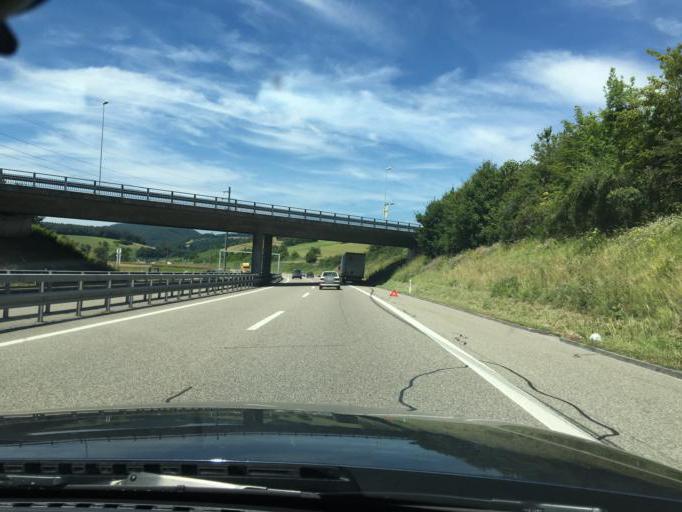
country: CH
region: Aargau
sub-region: Bezirk Aarau
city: Densbueren
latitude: 47.4830
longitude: 8.0959
